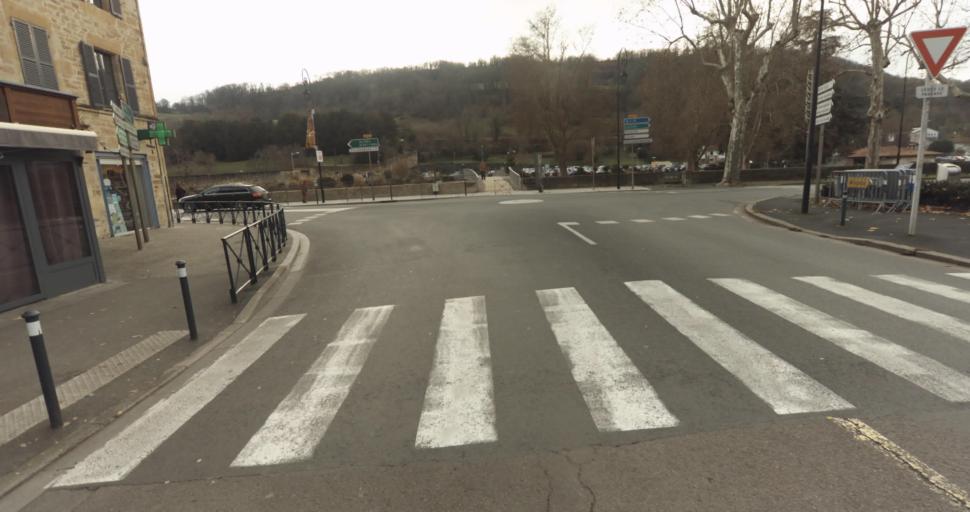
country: FR
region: Midi-Pyrenees
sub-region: Departement du Lot
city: Figeac
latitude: 44.6077
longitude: 2.0312
